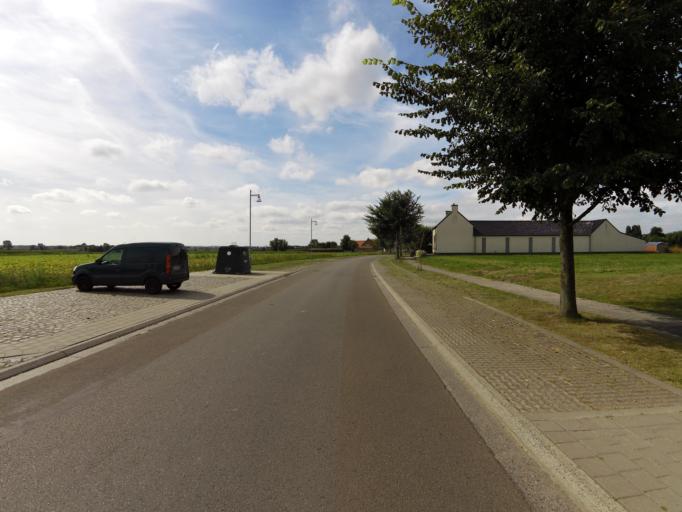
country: BE
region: Flanders
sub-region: Provincie West-Vlaanderen
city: Houthulst
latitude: 50.9335
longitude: 2.9288
